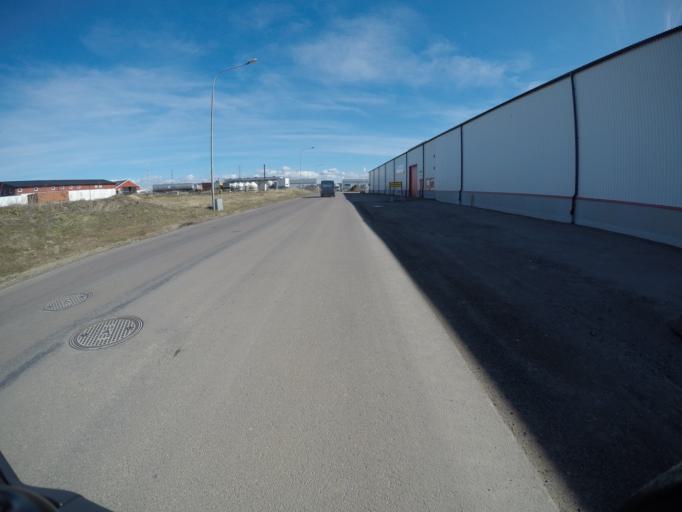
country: SE
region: Halland
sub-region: Laholms Kommun
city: Laholm
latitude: 56.4990
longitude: 13.0122
